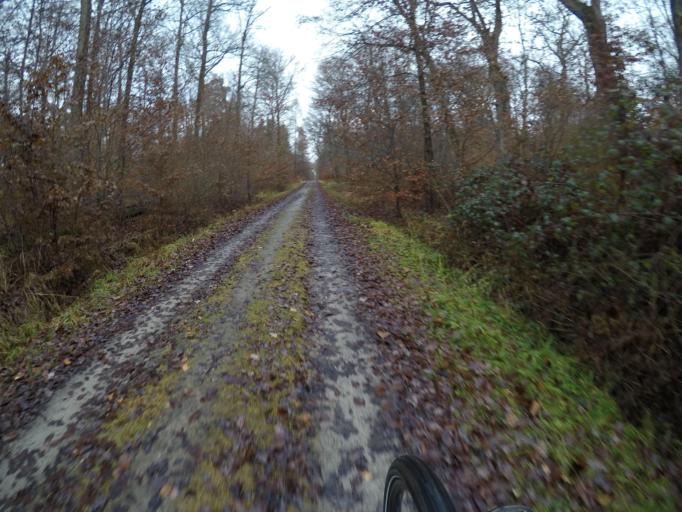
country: DE
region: Baden-Wuerttemberg
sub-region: Regierungsbezirk Stuttgart
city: Gerlingen
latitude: 48.7581
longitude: 9.0820
